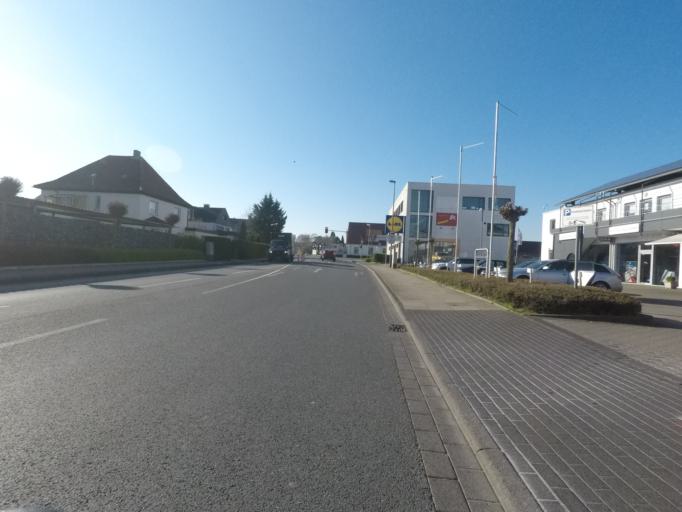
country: DE
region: North Rhine-Westphalia
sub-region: Regierungsbezirk Detmold
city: Bielefeld
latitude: 52.0128
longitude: 8.5984
